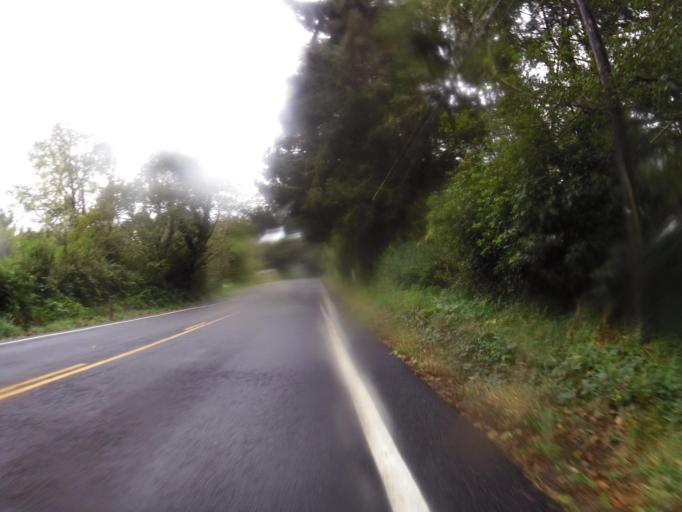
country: US
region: California
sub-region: Humboldt County
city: Westhaven-Moonstone
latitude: 41.1245
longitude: -124.1564
